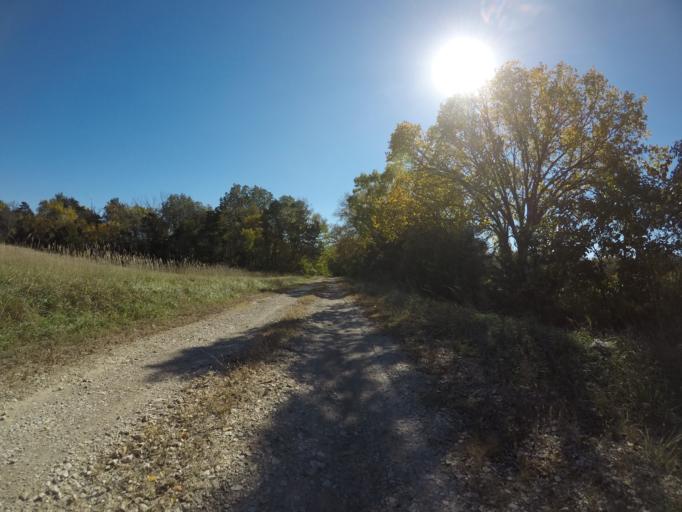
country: US
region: Kansas
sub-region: Wabaunsee County
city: Alma
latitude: 38.9816
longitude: -96.4555
